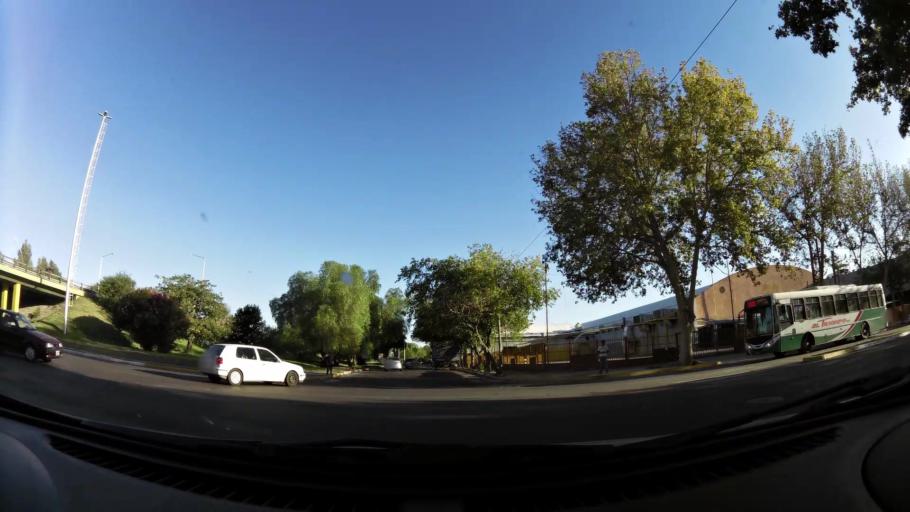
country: AR
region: San Juan
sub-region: Departamento de Santa Lucia
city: Santa Lucia
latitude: -31.5414
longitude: -68.5043
